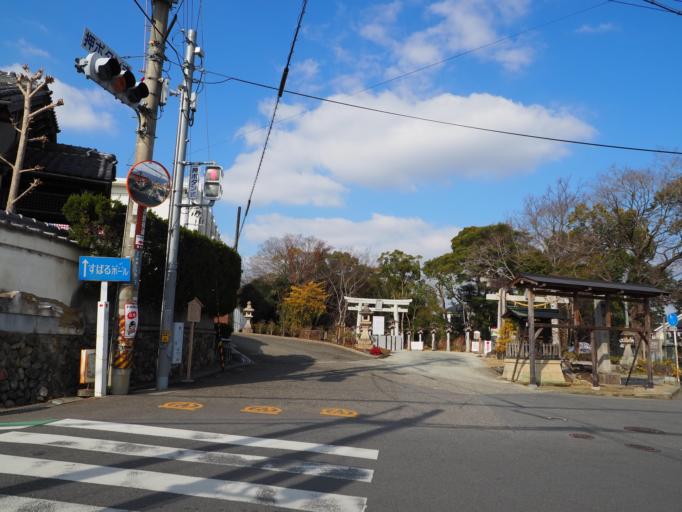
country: JP
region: Osaka
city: Tondabayashicho
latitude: 34.4930
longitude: 135.5886
